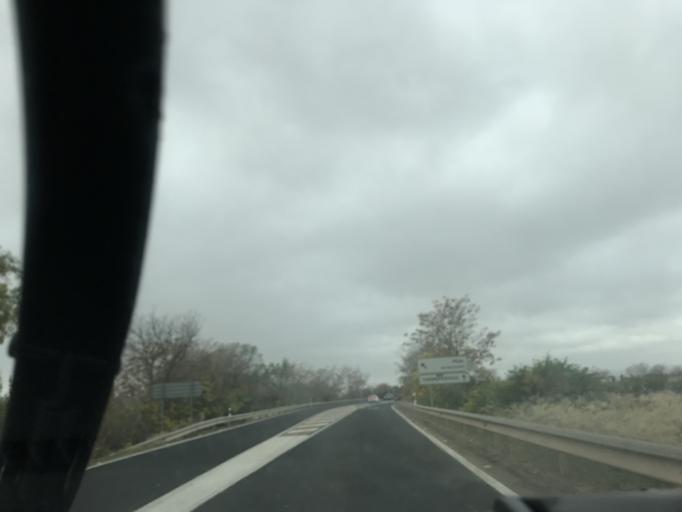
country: ES
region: Andalusia
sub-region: Provincia de Jaen
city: Peal de Becerro
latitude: 37.9142
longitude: -3.1024
